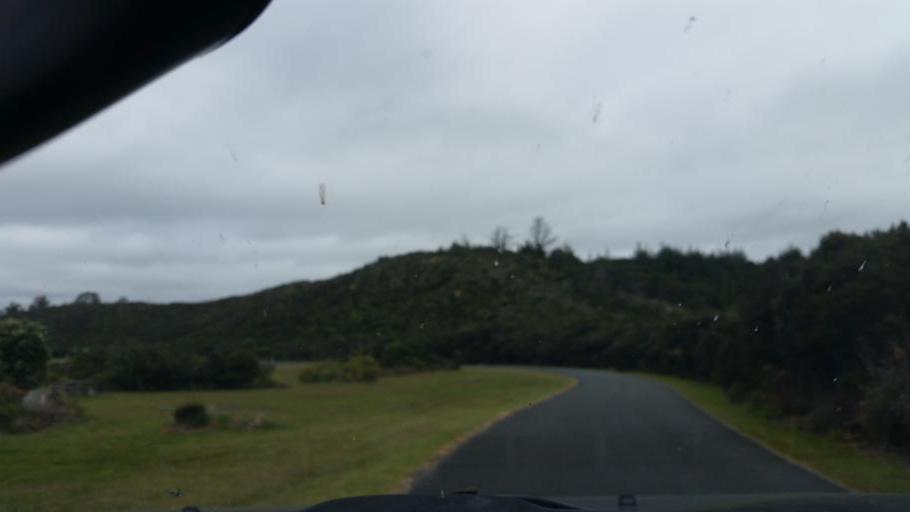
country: NZ
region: Northland
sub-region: Kaipara District
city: Dargaville
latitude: -35.8119
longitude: 173.6597
